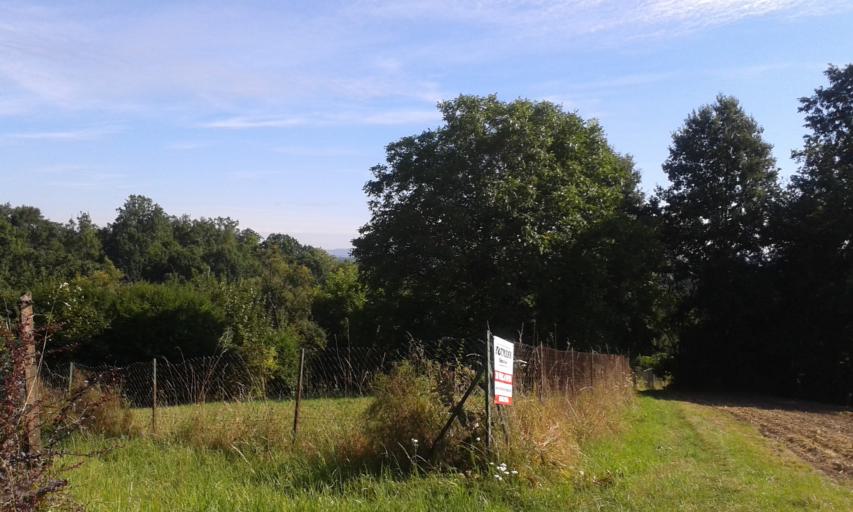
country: DE
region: Bavaria
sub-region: Upper Franconia
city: Bamberg
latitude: 49.8764
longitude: 10.8966
